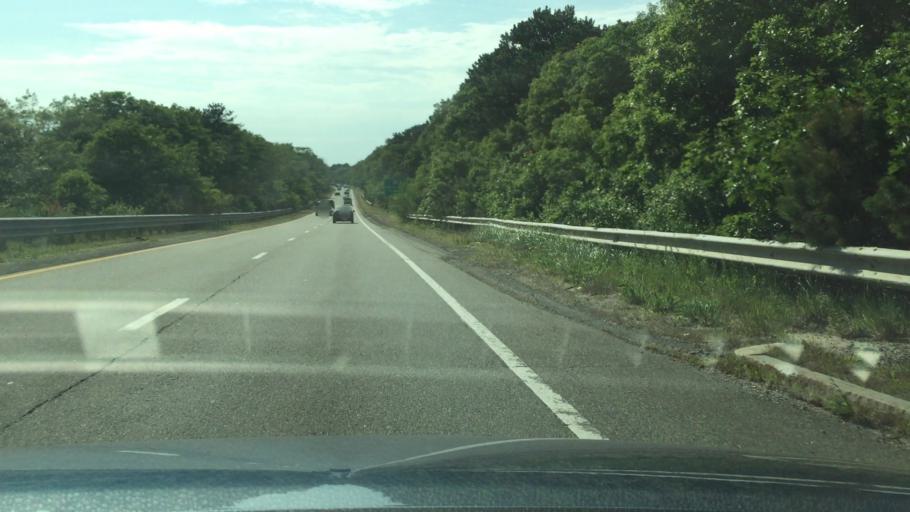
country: US
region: Massachusetts
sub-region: Barnstable County
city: Barnstable
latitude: 41.6887
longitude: -70.3074
